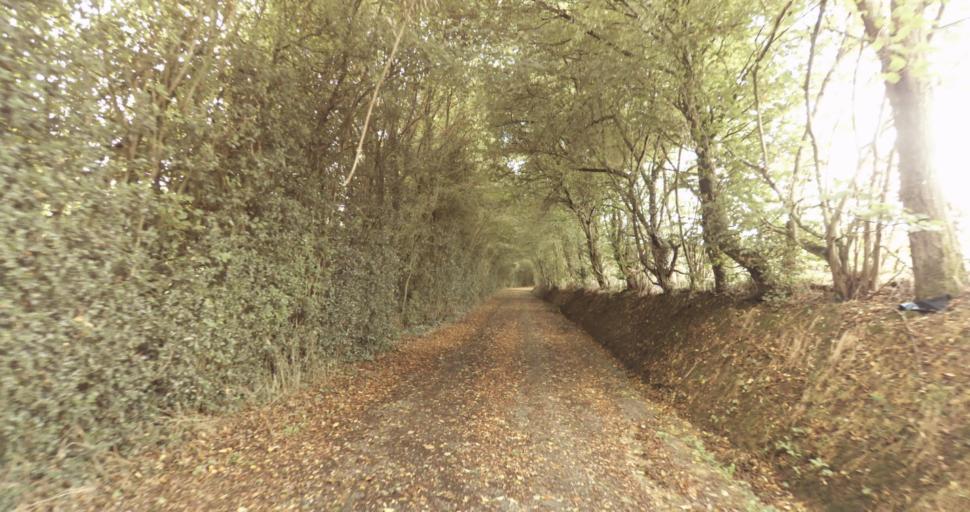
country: FR
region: Lower Normandy
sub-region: Departement de l'Orne
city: Sainte-Gauburge-Sainte-Colombe
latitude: 48.7066
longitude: 0.3927
